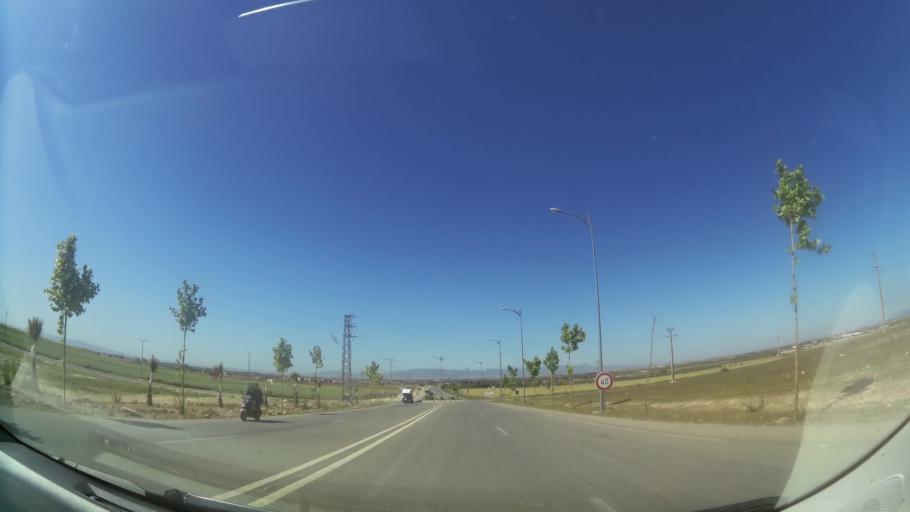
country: MA
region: Oriental
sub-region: Oujda-Angad
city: Oujda
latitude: 34.6867
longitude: -1.8575
